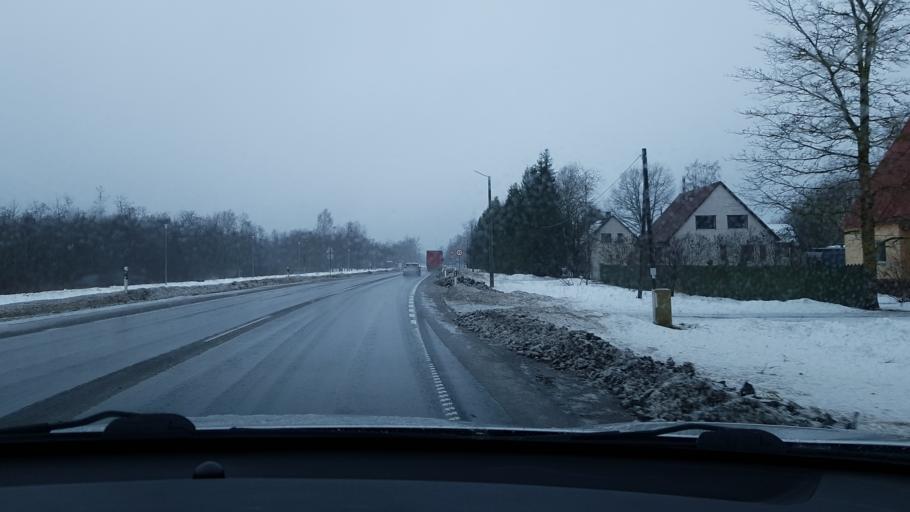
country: EE
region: Jaervamaa
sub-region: Tueri vald
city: Tueri
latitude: 58.8258
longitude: 25.4554
